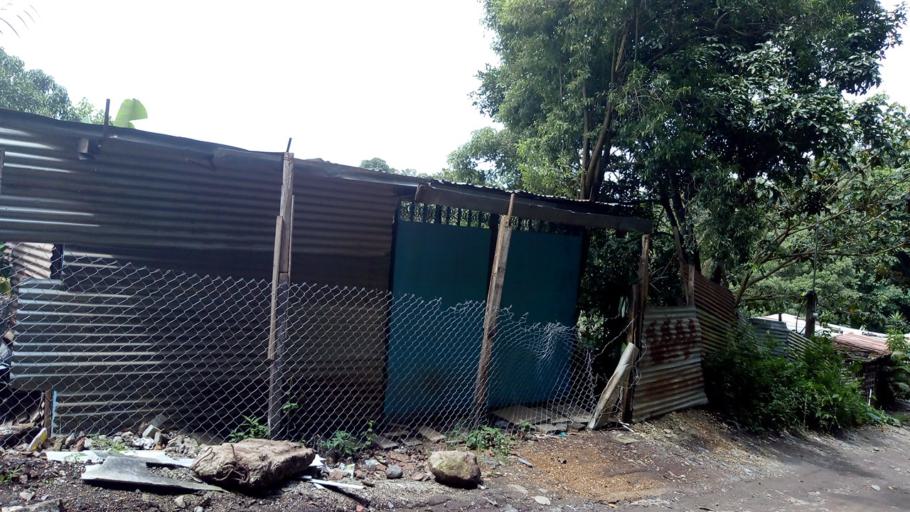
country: GT
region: Guatemala
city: Petapa
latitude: 14.5151
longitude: -90.5206
